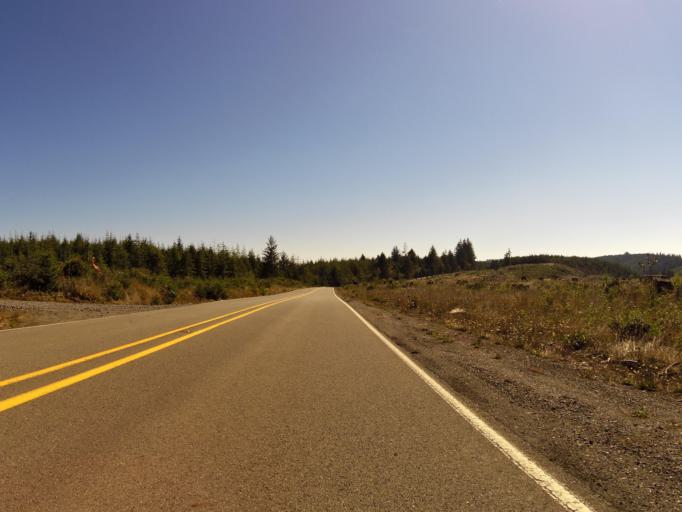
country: US
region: Oregon
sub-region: Coos County
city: Barview
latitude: 43.2575
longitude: -124.3381
